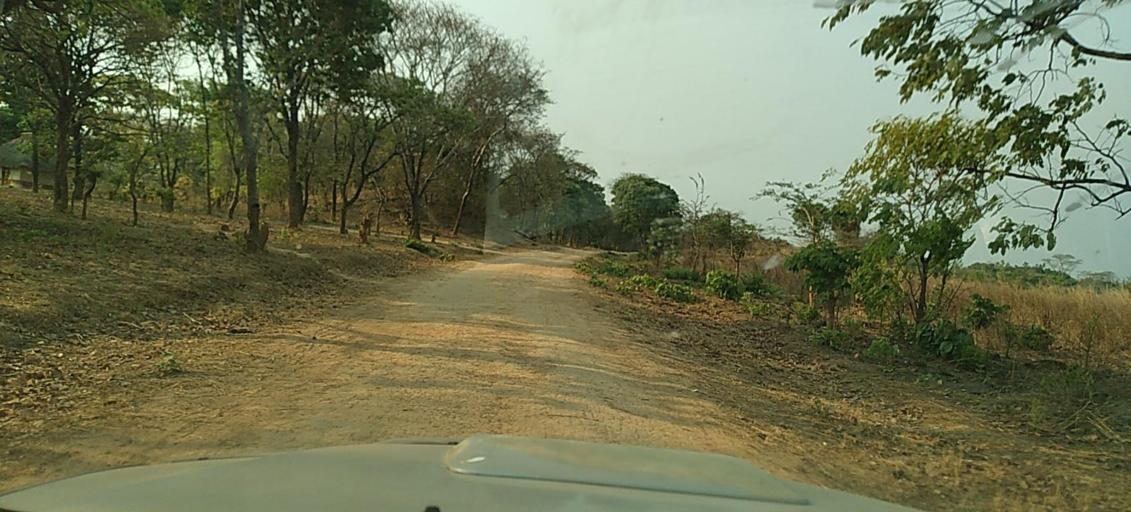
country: ZM
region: North-Western
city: Kasempa
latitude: -13.2810
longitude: 26.5550
